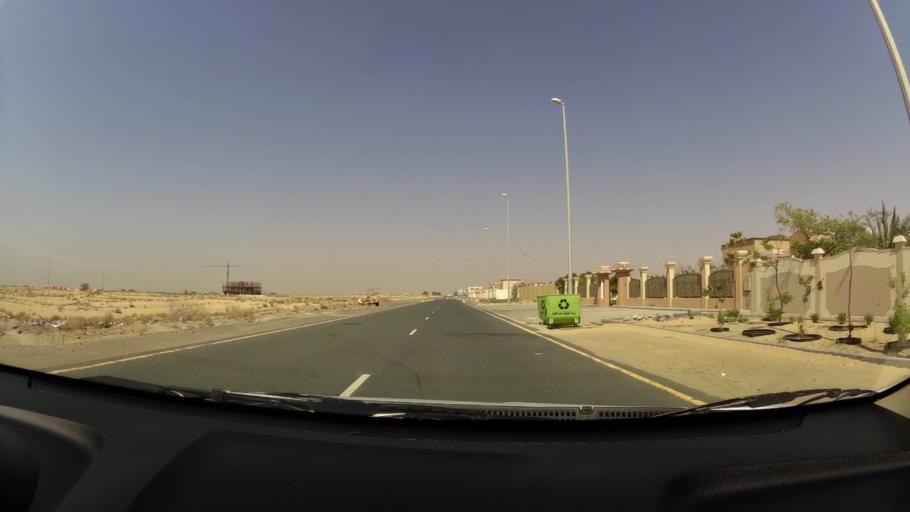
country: AE
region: Umm al Qaywayn
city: Umm al Qaywayn
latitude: 25.4915
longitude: 55.6031
